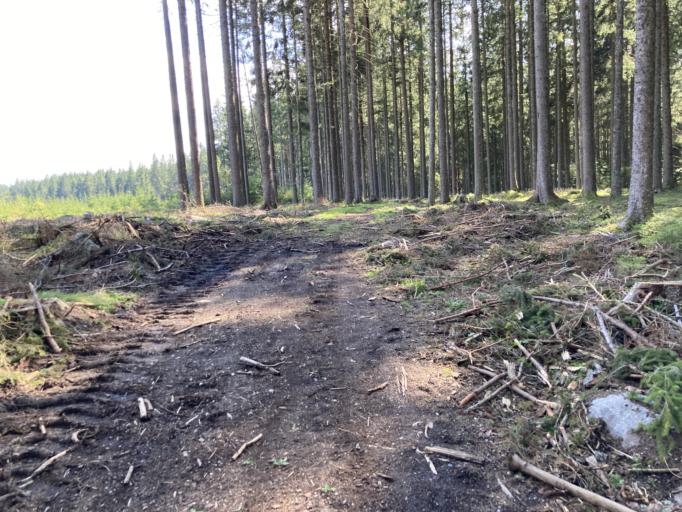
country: DE
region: Baden-Wuerttemberg
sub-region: Freiburg Region
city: Schonwald im Schwarzwald
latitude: 48.1089
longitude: 8.2235
